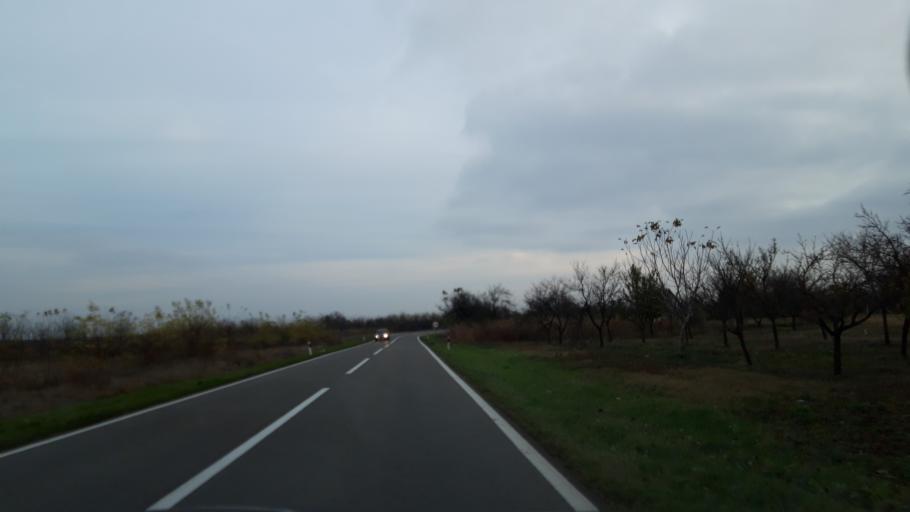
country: RS
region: Autonomna Pokrajina Vojvodina
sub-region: Severnobanatski Okrug
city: Coka
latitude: 45.9628
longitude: 20.1314
